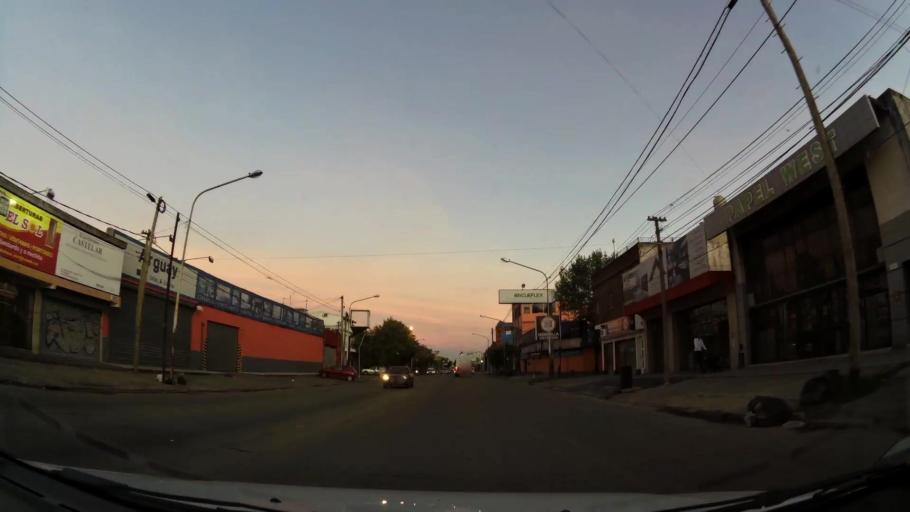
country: AR
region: Buenos Aires
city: Ituzaingo
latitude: -34.6576
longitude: -58.6437
